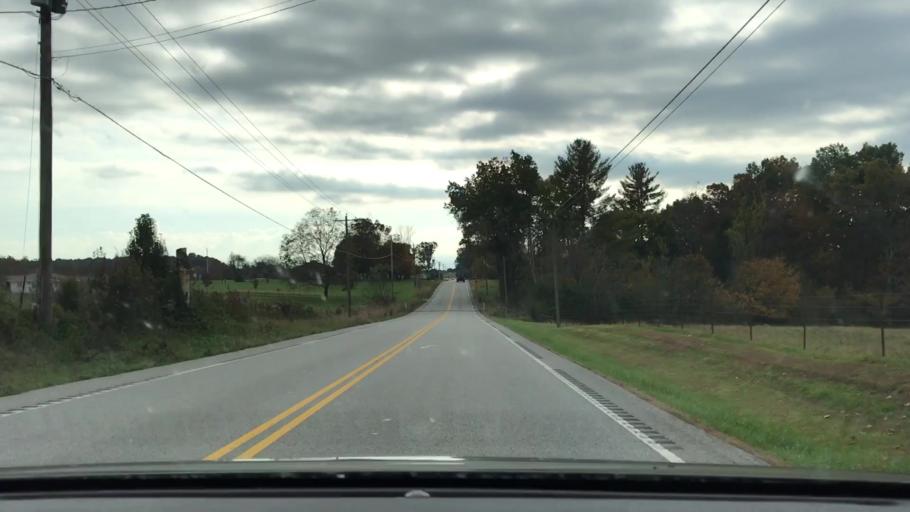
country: US
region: Tennessee
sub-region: Fentress County
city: Jamestown
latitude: 36.3645
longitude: -84.8435
